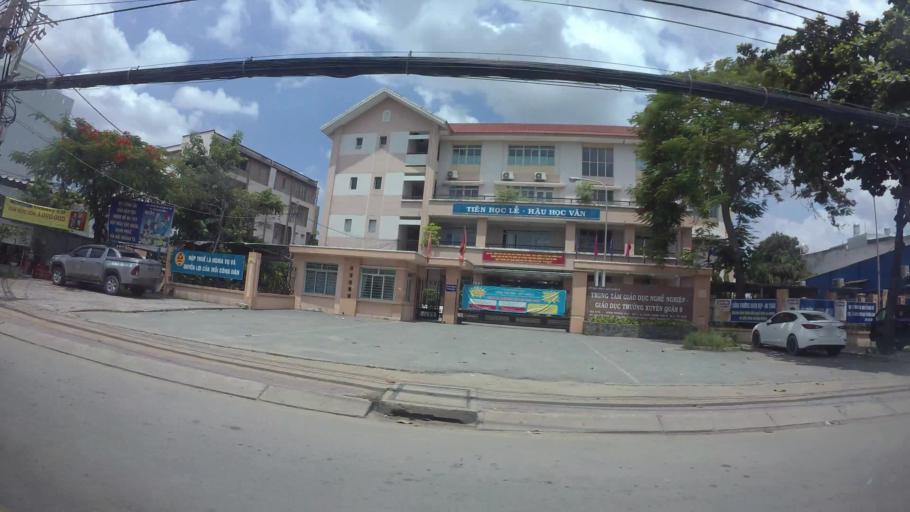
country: VN
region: Ho Chi Minh City
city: Quan Chin
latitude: 10.8387
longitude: 106.7806
